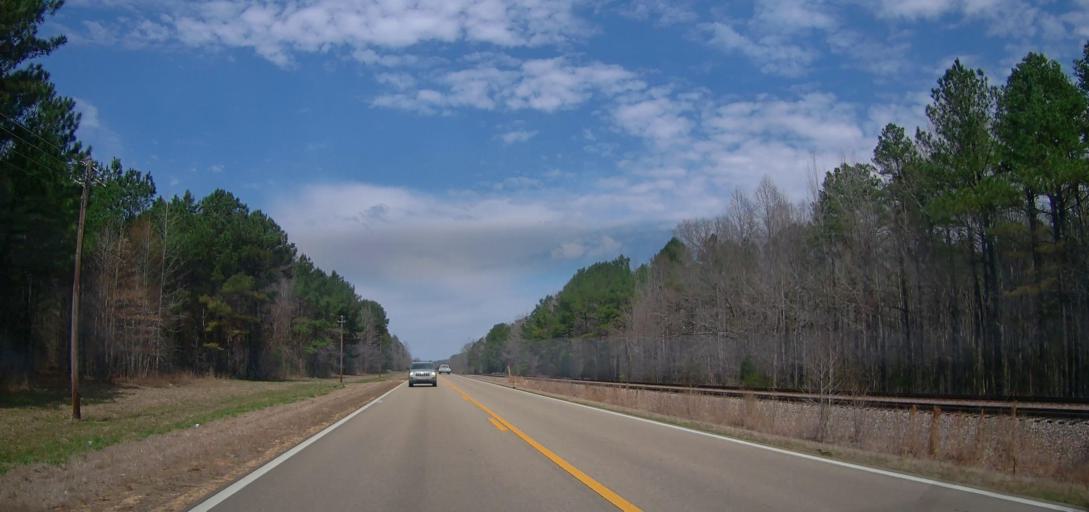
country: US
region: Mississippi
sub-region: Union County
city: New Albany
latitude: 34.5848
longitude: -89.1328
